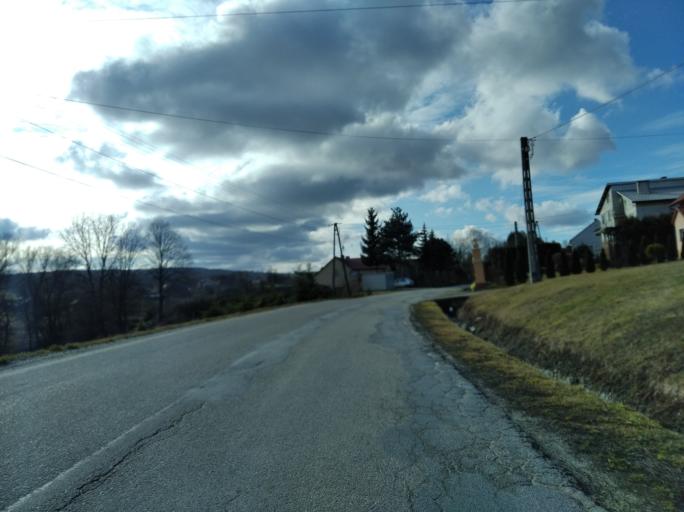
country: PL
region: Subcarpathian Voivodeship
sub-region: Powiat strzyzowski
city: Wisniowa
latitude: 49.9125
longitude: 21.6959
